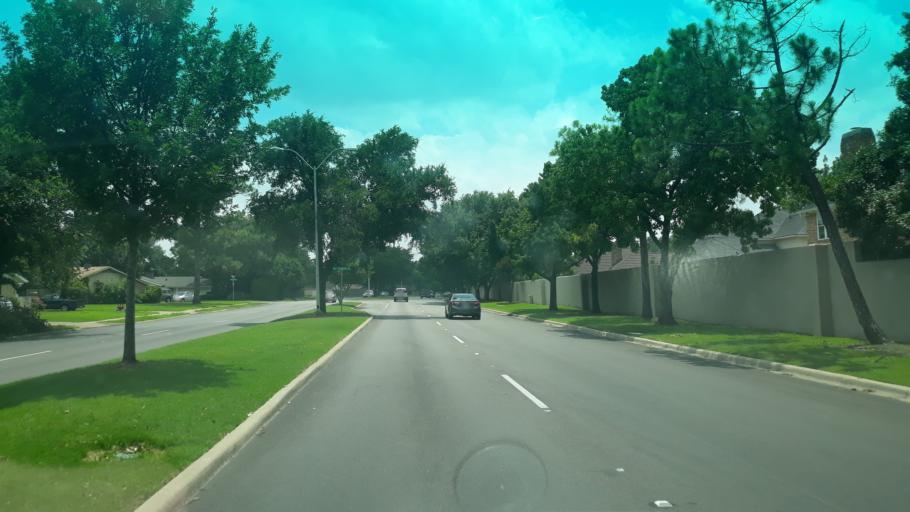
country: US
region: Texas
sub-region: Dallas County
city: Irving
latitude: 32.8581
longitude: -96.9616
